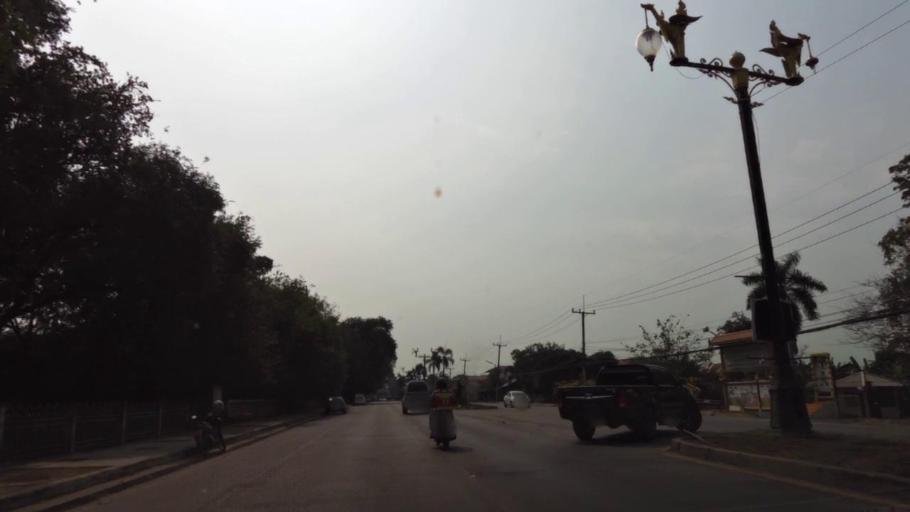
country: TH
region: Phra Nakhon Si Ayutthaya
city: Phra Nakhon Si Ayutthaya
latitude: 14.3506
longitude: 100.5680
